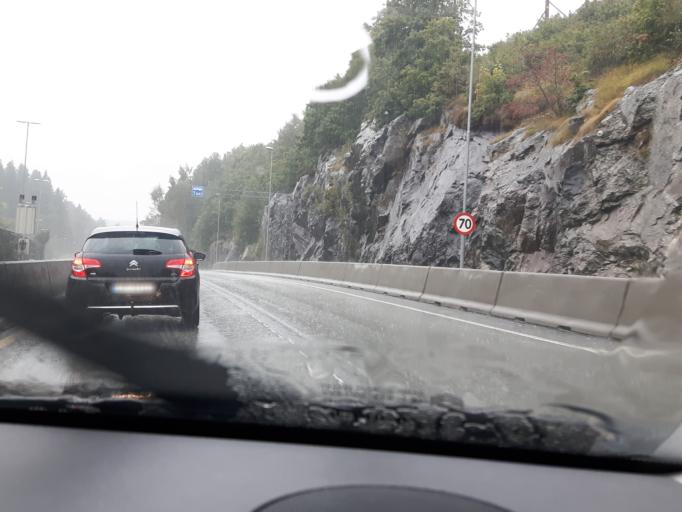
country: NO
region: Vest-Agder
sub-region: Kristiansand
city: Strai
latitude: 58.1440
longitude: 7.9309
